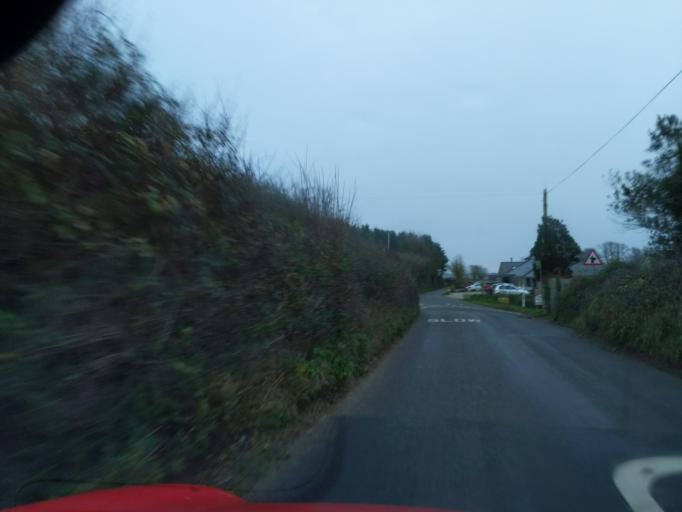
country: GB
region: England
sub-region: Devon
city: Wembury
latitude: 50.3300
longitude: -4.0635
